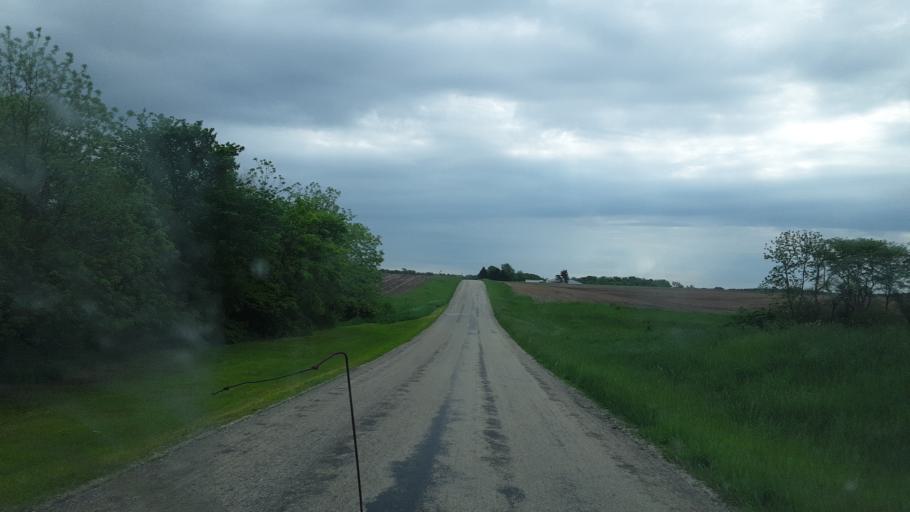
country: US
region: Illinois
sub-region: Fulton County
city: Astoria
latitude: 40.3645
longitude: -90.4668
